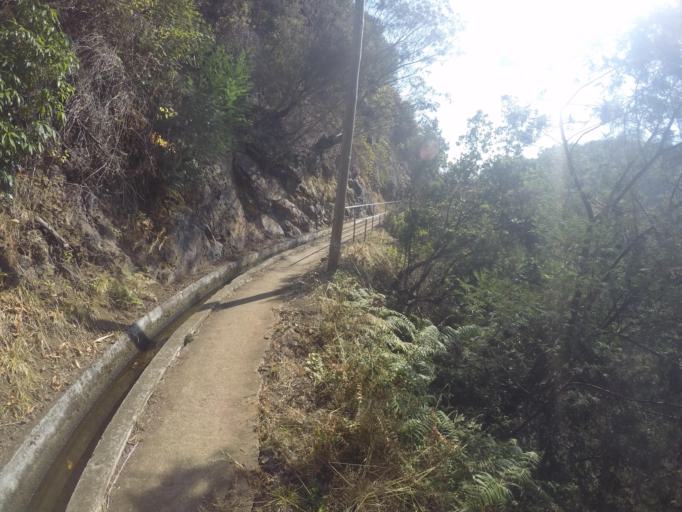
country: PT
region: Madeira
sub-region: Santana
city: Santana
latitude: 32.7667
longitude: -16.8191
